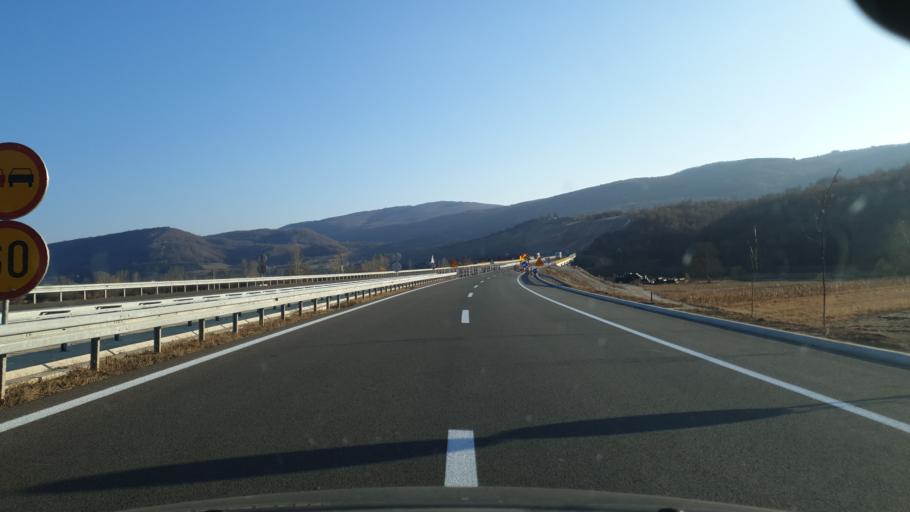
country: RS
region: Central Serbia
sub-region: Pirotski Okrug
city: Dimitrovgrad
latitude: 43.0136
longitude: 22.8025
